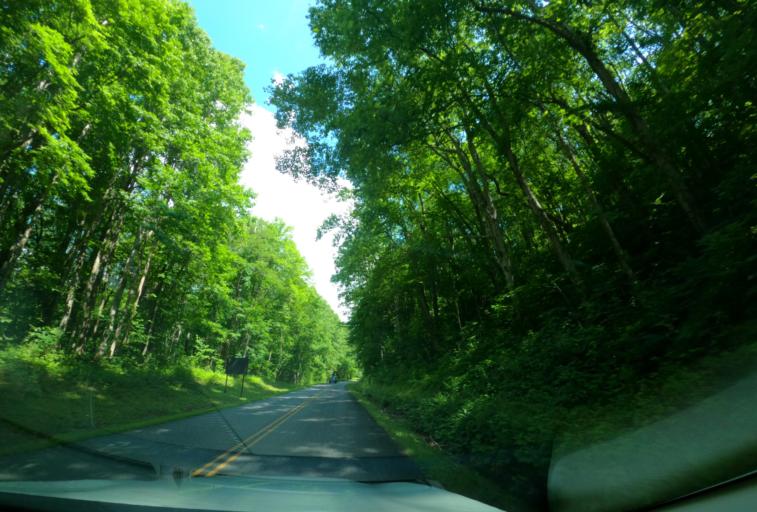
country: US
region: North Carolina
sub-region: Haywood County
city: Maggie Valley
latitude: 35.4416
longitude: -83.0804
